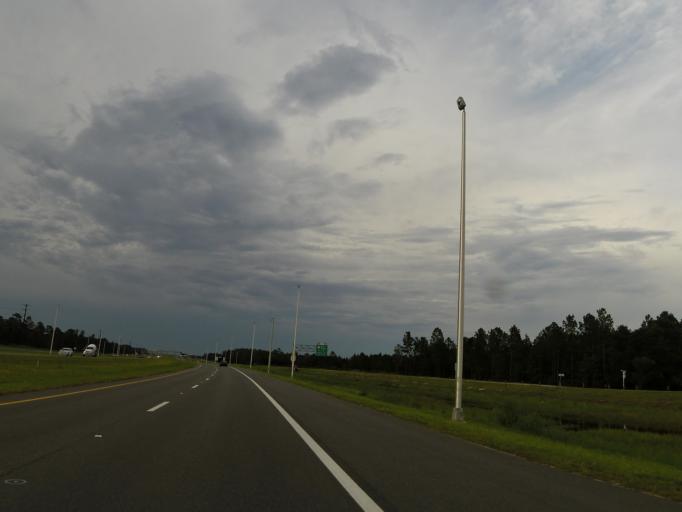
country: US
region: Florida
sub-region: Clay County
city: Middleburg
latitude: 30.1193
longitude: -81.8304
